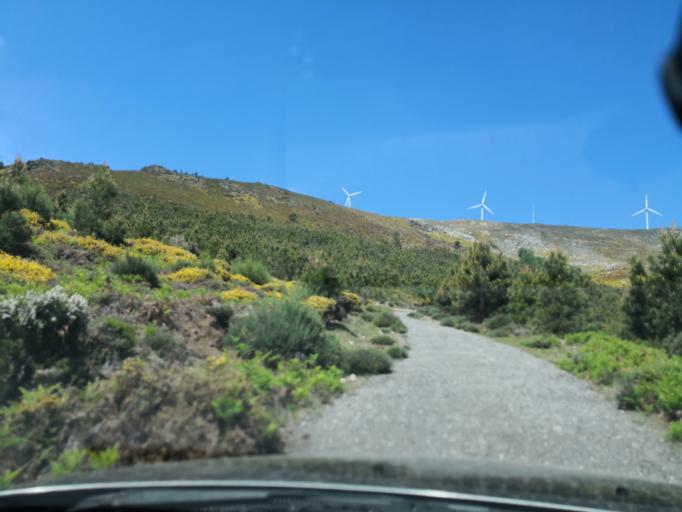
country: PT
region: Vila Real
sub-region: Vila Real
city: Vila Real
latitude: 41.3664
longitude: -7.7422
